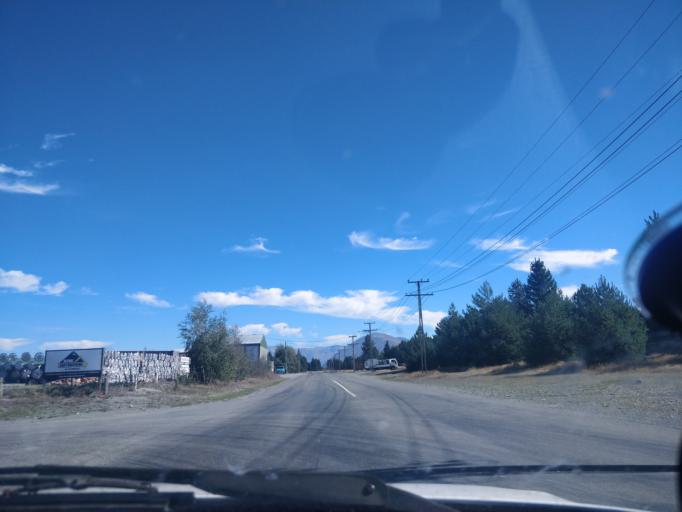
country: NZ
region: Otago
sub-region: Queenstown-Lakes District
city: Wanaka
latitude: -44.2646
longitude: 170.0895
